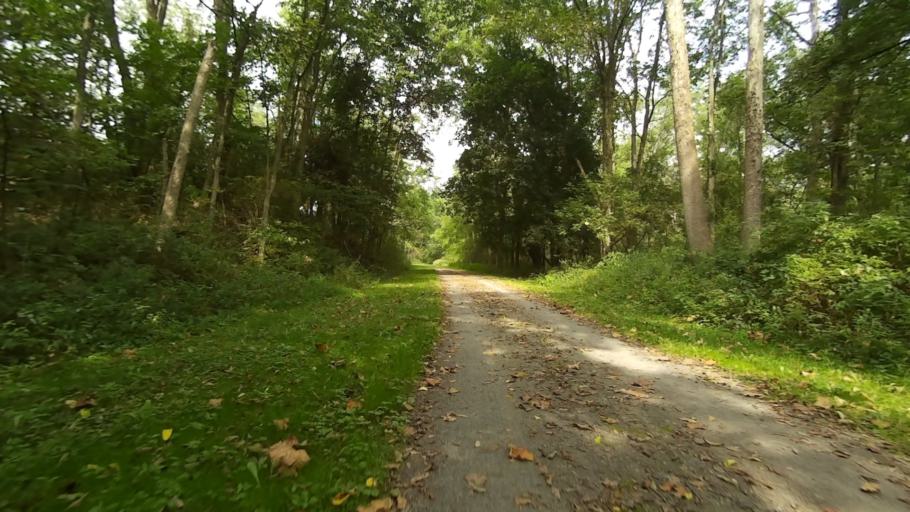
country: US
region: Pennsylvania
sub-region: Blair County
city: Williamsburg
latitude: 40.5188
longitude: -78.1698
